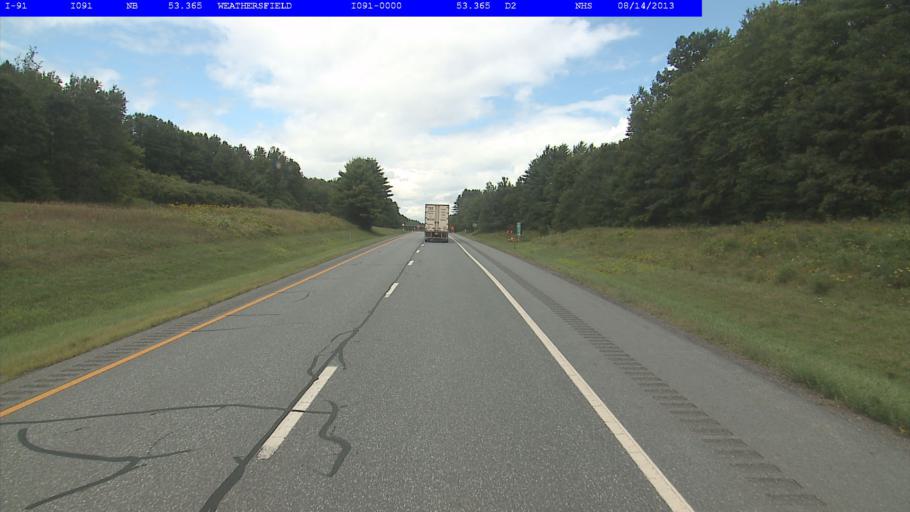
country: US
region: Vermont
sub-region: Windsor County
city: Windsor
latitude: 43.4285
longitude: -72.4027
